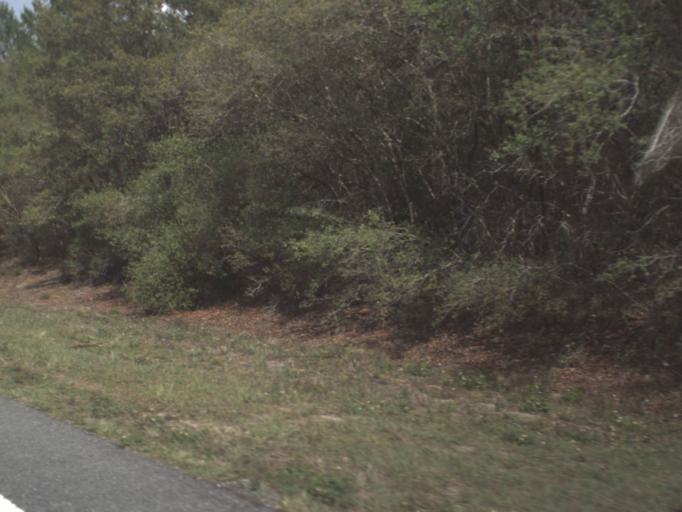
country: US
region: Florida
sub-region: Lake County
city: Astor
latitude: 29.1585
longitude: -81.5922
